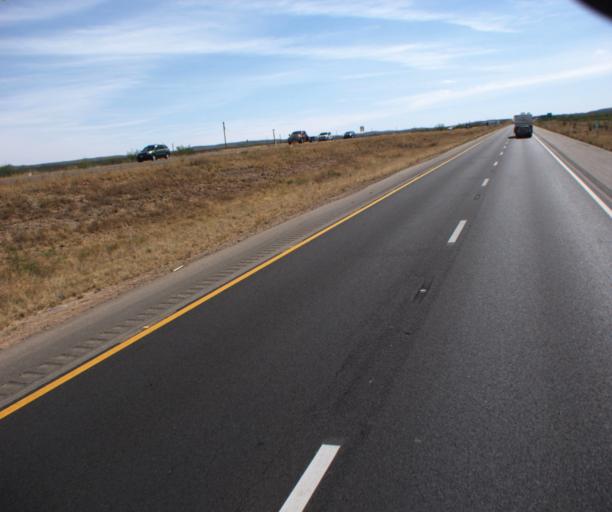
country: US
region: Arizona
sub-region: Cochise County
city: Mescal
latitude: 31.9842
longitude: -110.5547
